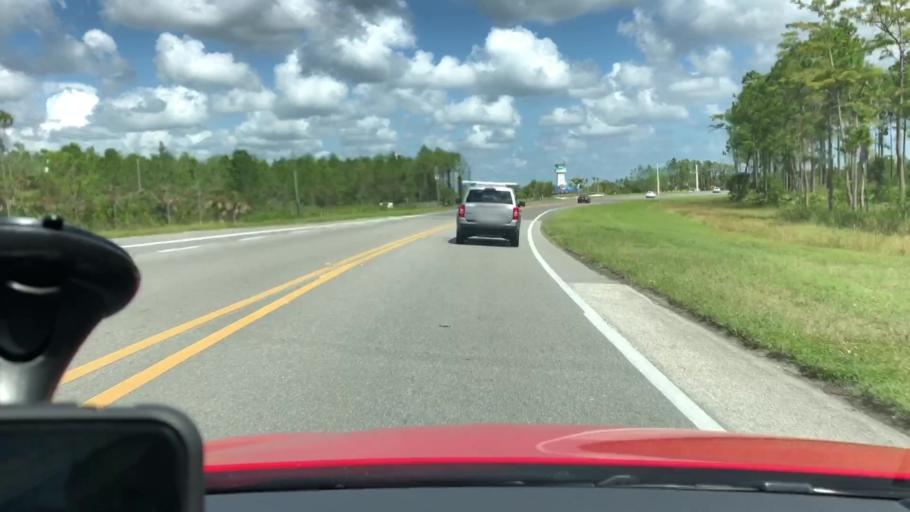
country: US
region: Florida
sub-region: Volusia County
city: Holly Hill
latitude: 29.2102
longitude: -81.1197
